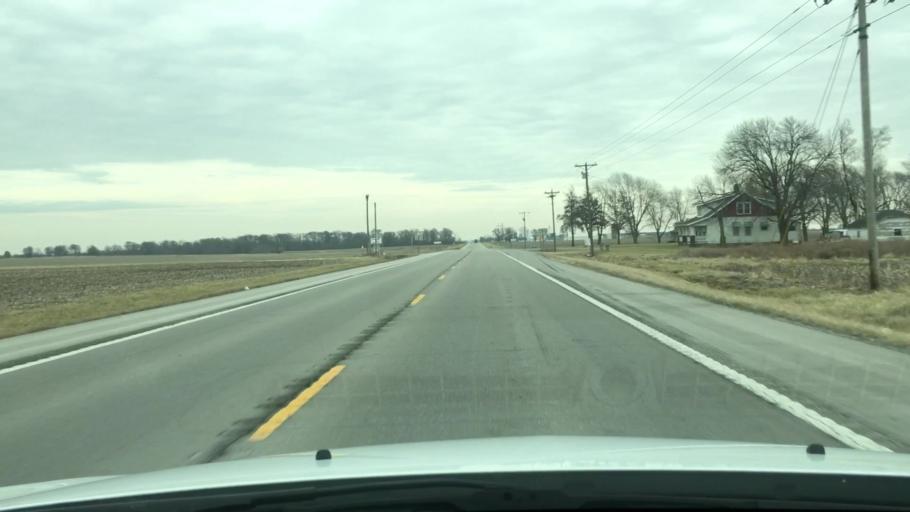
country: US
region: Missouri
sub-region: Audrain County
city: Mexico
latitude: 39.1638
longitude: -91.7635
